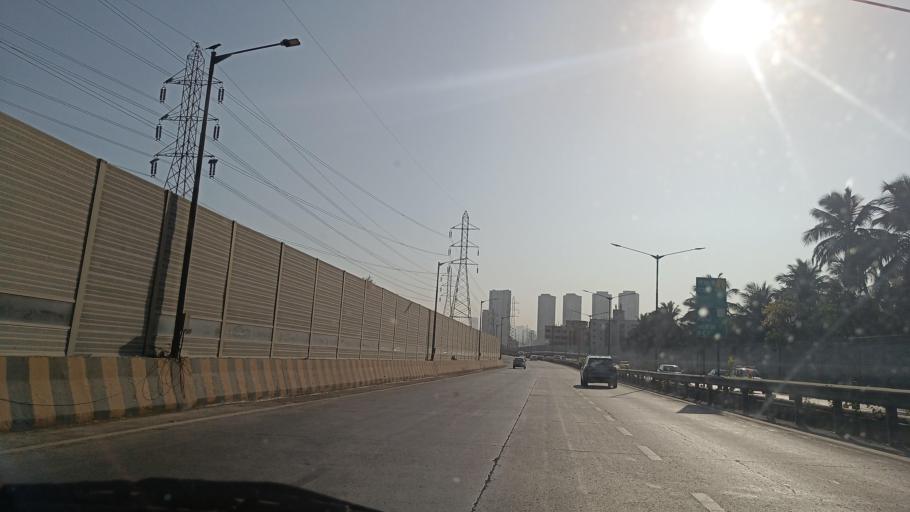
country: IN
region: Maharashtra
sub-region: Mumbai Suburban
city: Mumbai
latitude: 19.0313
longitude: 72.8920
